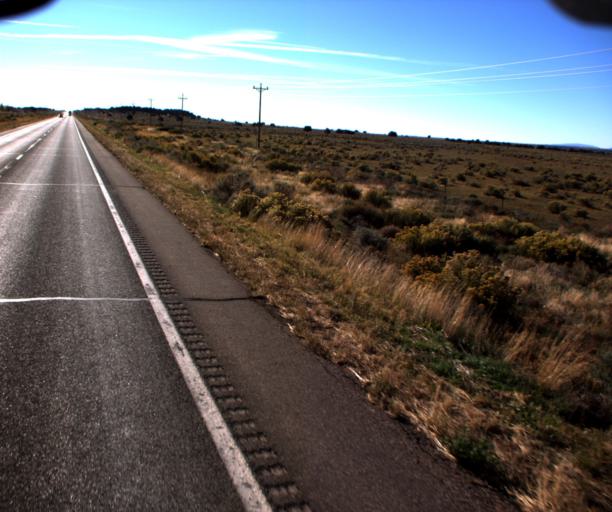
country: US
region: Arizona
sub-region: Mohave County
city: Colorado City
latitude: 36.9800
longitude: -112.9827
